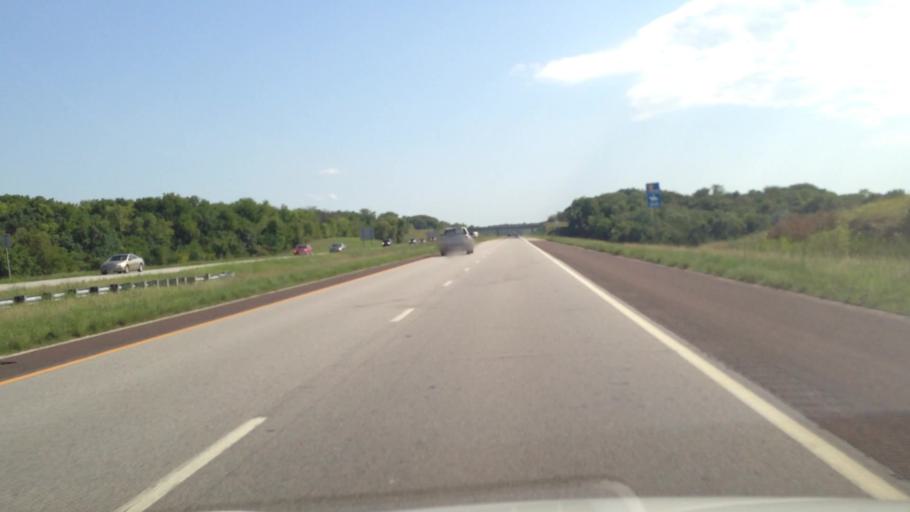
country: US
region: Kansas
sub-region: Miami County
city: Louisburg
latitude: 38.6138
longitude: -94.6949
